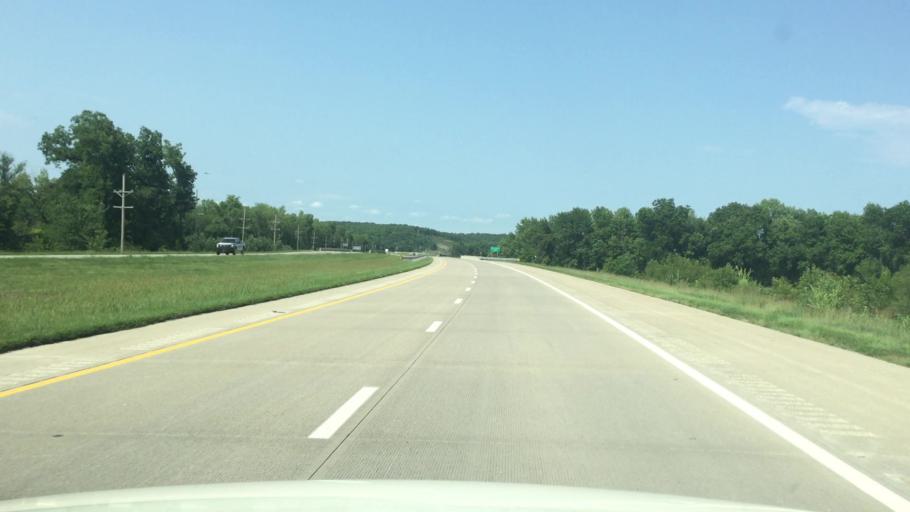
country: US
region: Kansas
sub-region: Linn County
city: Pleasanton
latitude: 38.2338
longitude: -94.6916
